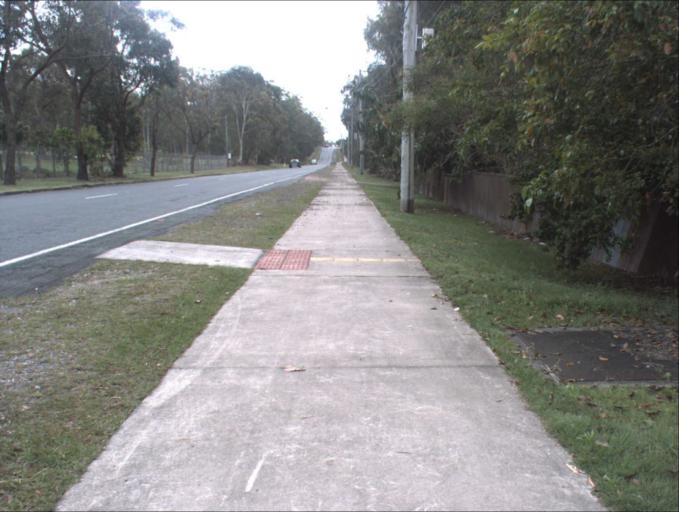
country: AU
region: Queensland
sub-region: Logan
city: Logan Reserve
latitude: -27.7012
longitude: 153.0764
